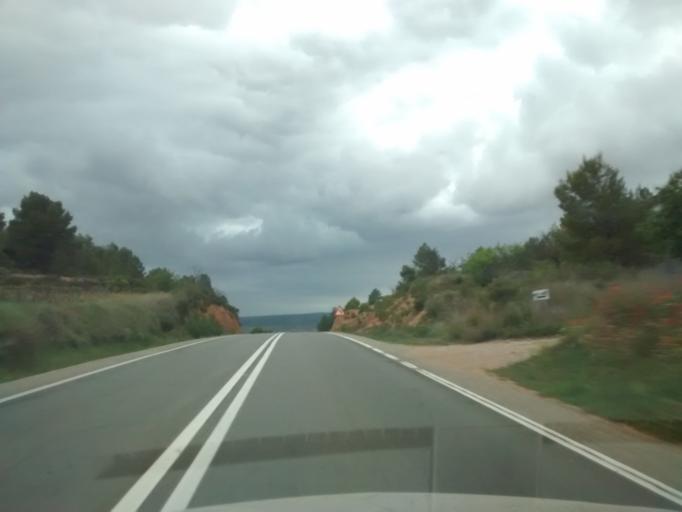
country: ES
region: Catalonia
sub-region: Provincia de Tarragona
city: Gandesa
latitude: 41.0444
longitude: 0.4528
